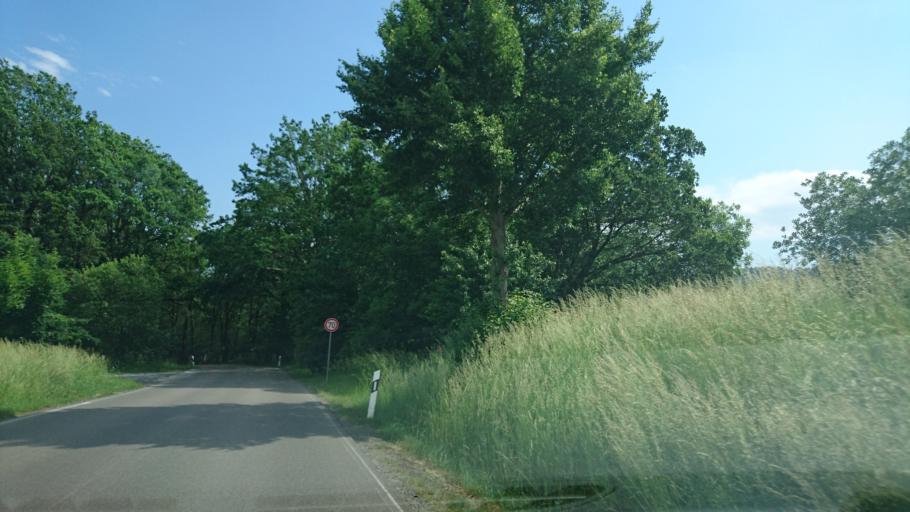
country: DE
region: Saxony
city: Dohma
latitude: 50.9102
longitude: 13.9719
